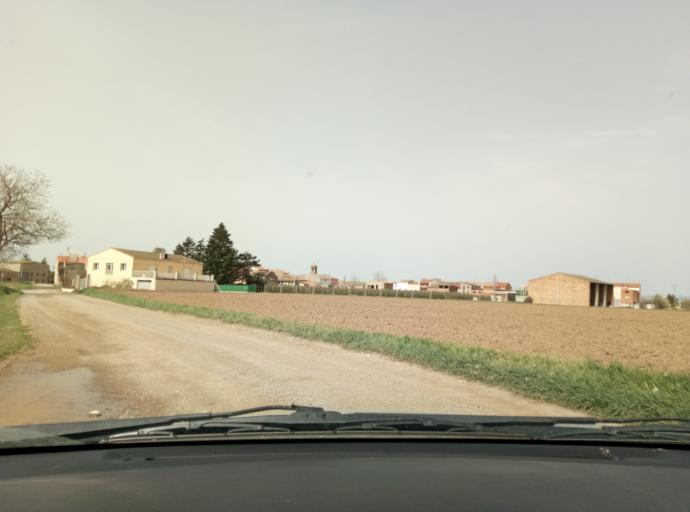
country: ES
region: Catalonia
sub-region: Provincia de Lleida
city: La Fuliola
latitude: 41.7137
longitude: 1.0239
